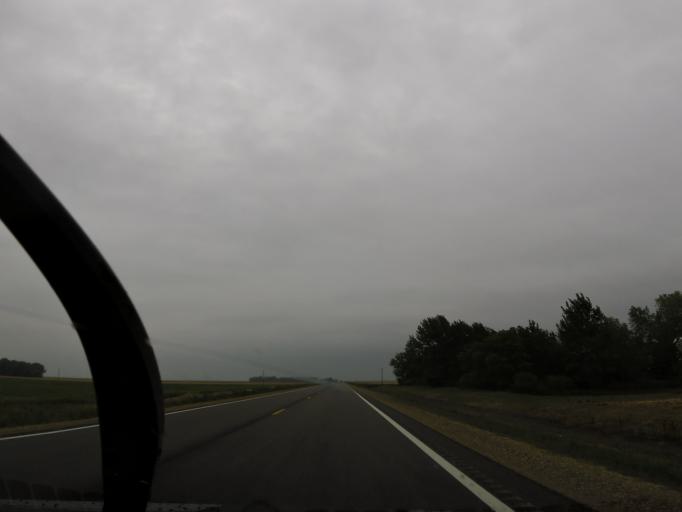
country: US
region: Minnesota
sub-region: Kittson County
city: Hallock
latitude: 48.4565
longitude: -96.9805
